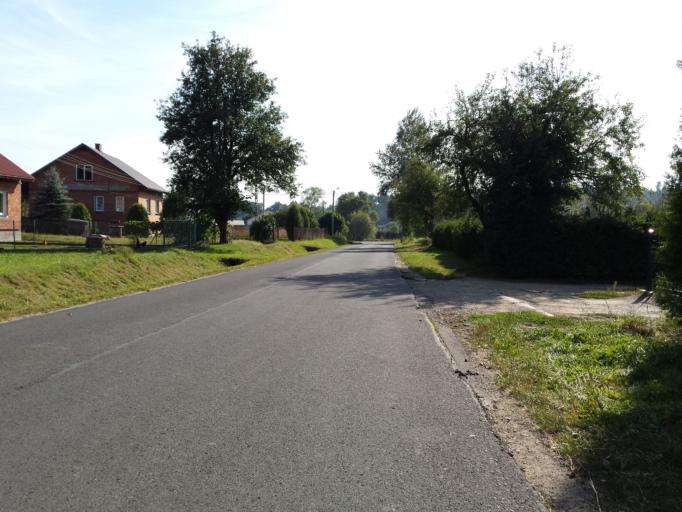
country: PL
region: Subcarpathian Voivodeship
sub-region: Powiat leski
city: Olszanica
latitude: 49.4889
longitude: 22.4458
